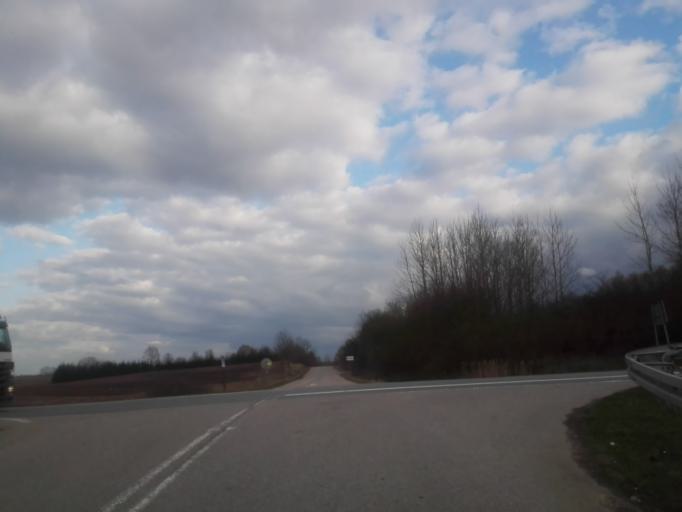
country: PL
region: Podlasie
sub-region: Suwalki
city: Suwalki
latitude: 54.1884
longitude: 23.0062
